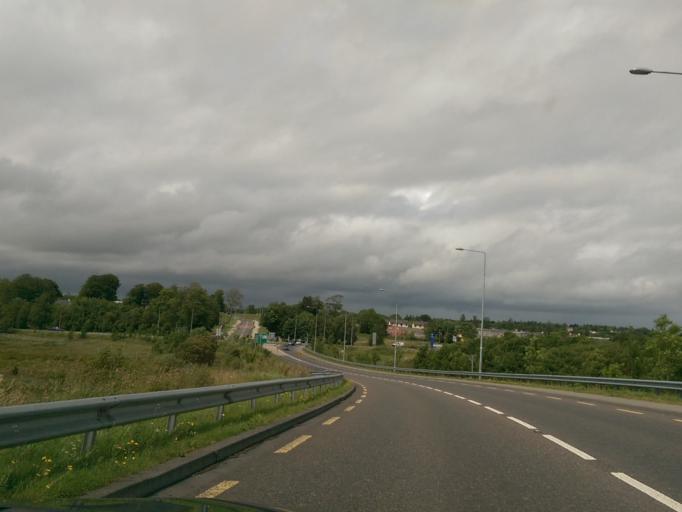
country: IE
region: Munster
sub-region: An Clar
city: Ennis
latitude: 52.8273
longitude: -8.9950
